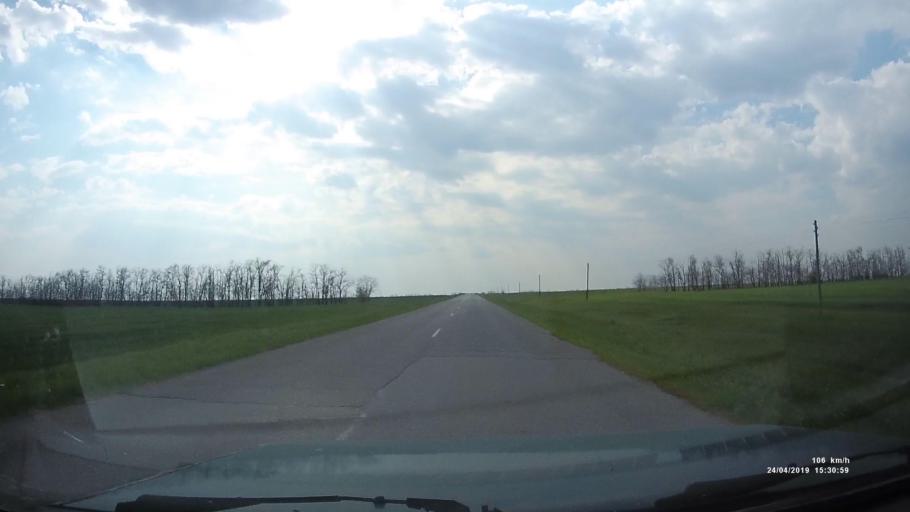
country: RU
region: Rostov
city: Remontnoye
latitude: 46.5998
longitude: 42.9938
